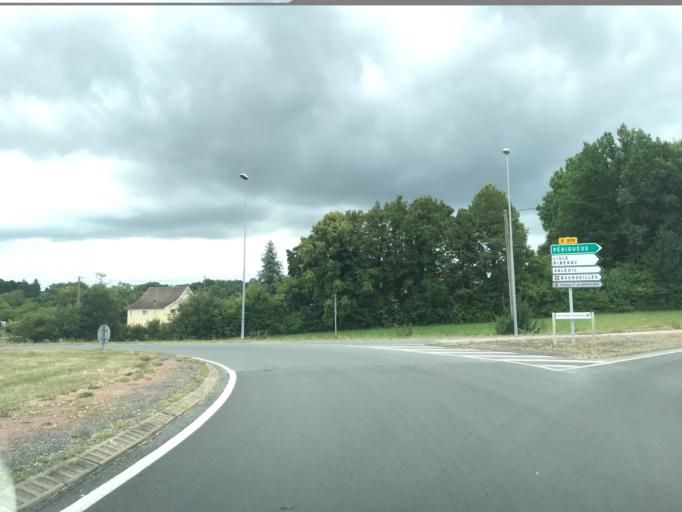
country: FR
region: Aquitaine
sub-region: Departement de la Dordogne
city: Brantome
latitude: 45.3779
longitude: 0.6419
